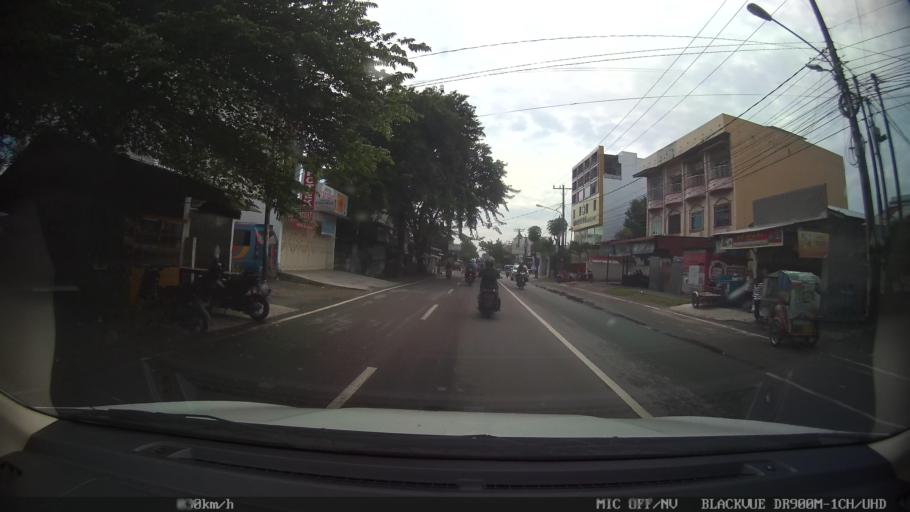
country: ID
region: North Sumatra
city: Medan
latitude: 3.6225
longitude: 98.6997
